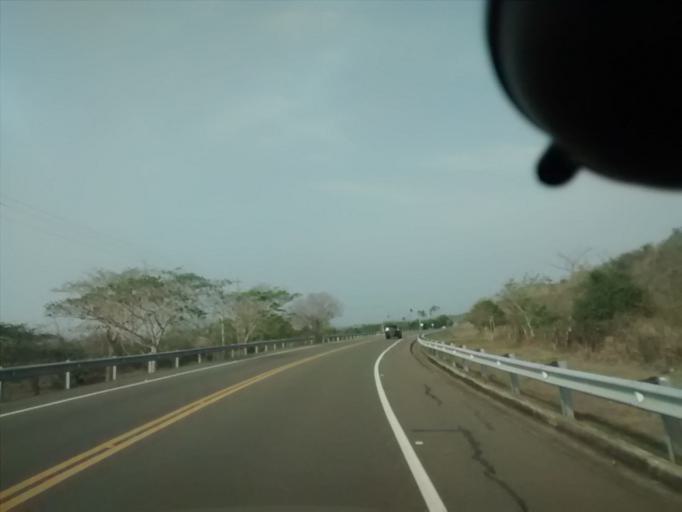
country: CO
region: Bolivar
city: Clemencia
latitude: 10.6354
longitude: -75.4191
